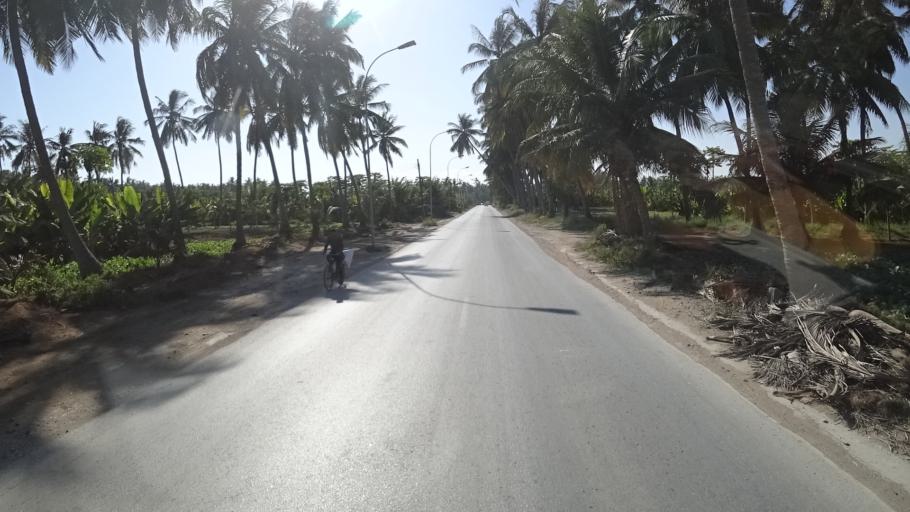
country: OM
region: Zufar
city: Salalah
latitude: 17.0128
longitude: 54.1176
